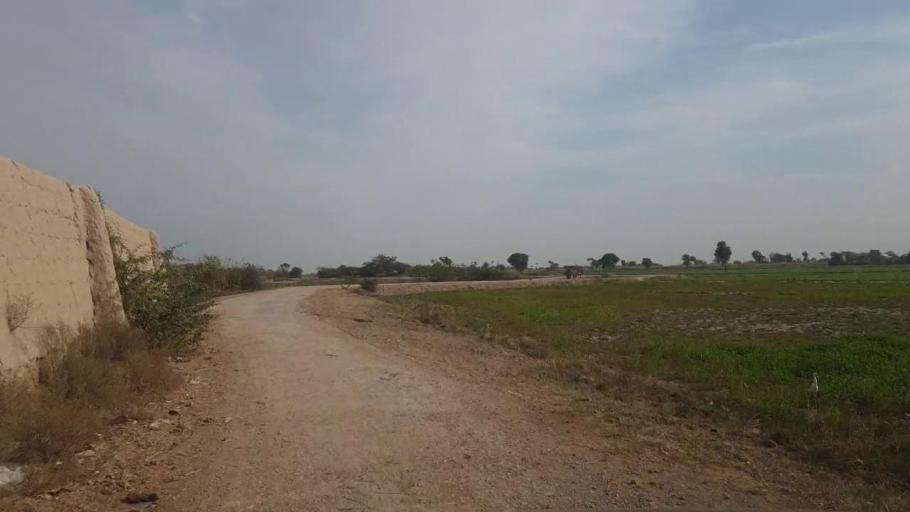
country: PK
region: Sindh
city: Nawabshah
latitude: 26.0919
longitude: 68.4862
